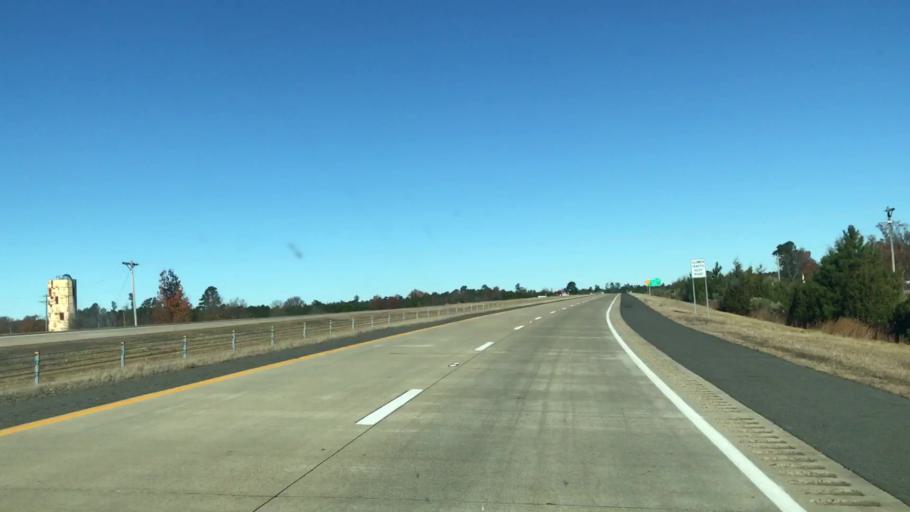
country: US
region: Texas
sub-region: Bowie County
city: Texarkana
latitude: 33.2547
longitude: -93.8935
